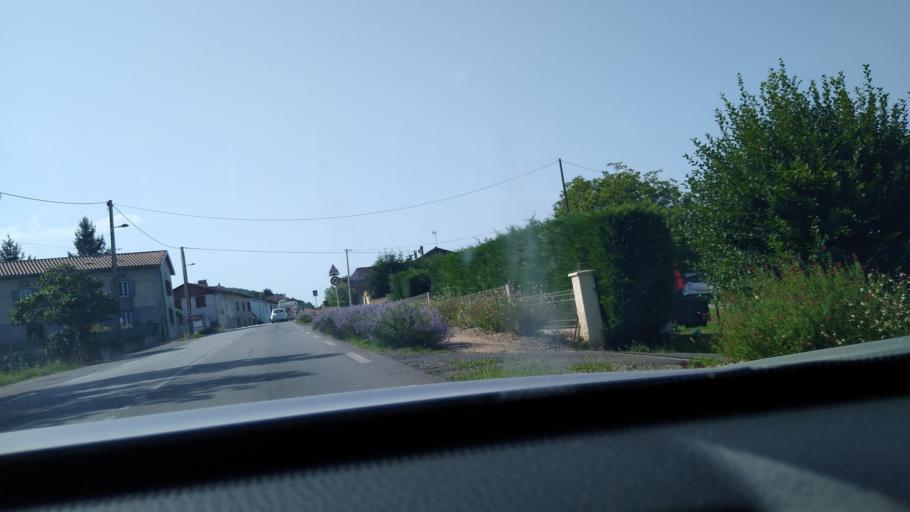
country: FR
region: Midi-Pyrenees
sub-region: Departement de l'Ariege
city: Saint-Lizier
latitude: 43.0269
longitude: 1.0888
